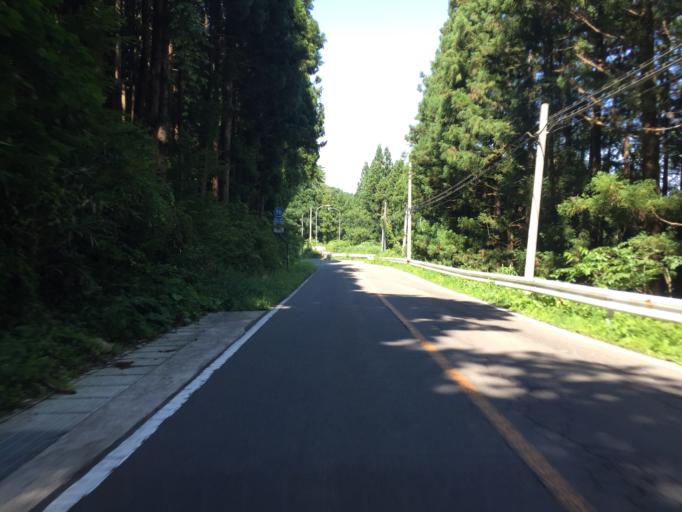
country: JP
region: Fukushima
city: Fukushima-shi
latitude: 37.7511
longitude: 140.3457
